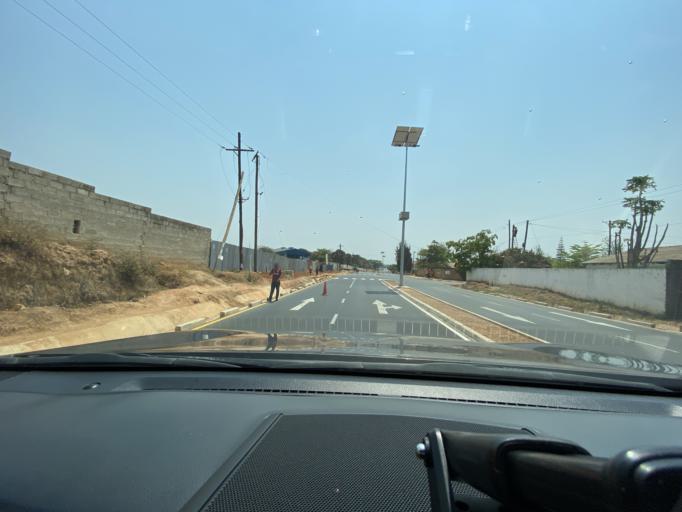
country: ZM
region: Lusaka
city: Lusaka
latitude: -15.3678
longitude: 28.3465
